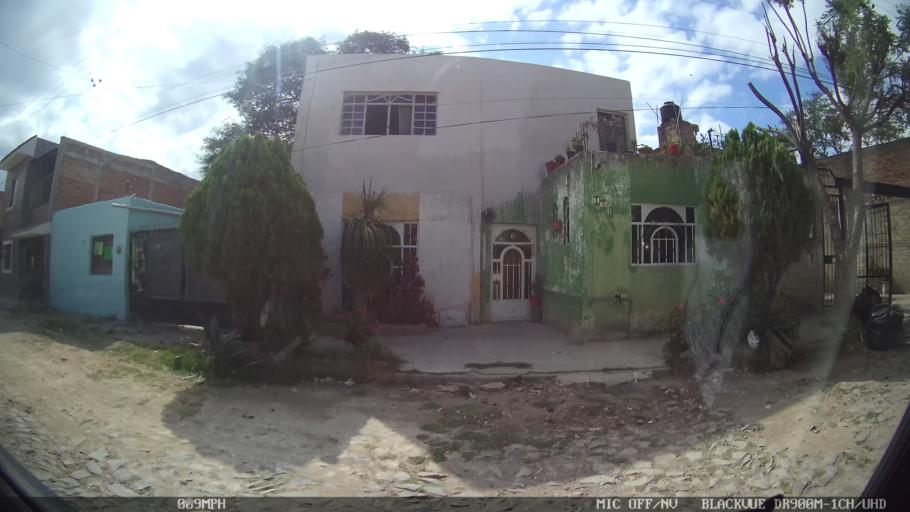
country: MX
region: Jalisco
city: Tlaquepaque
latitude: 20.6827
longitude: -103.2551
